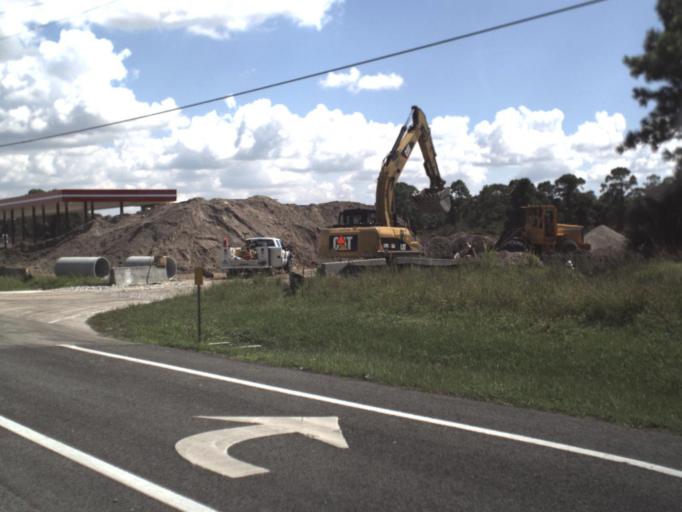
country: US
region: Florida
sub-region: Lee County
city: Palmona Park
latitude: 26.6822
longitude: -81.9070
